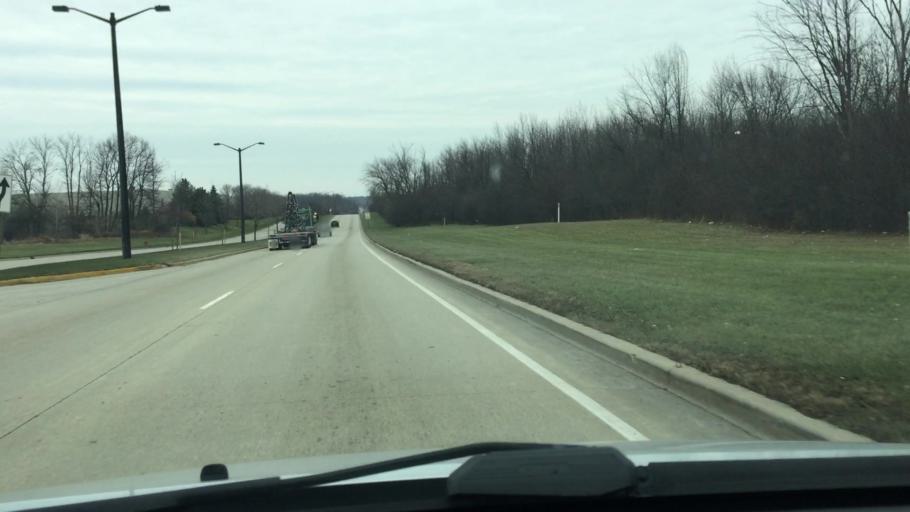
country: US
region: Wisconsin
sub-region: Waukesha County
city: Menomonee Falls
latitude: 43.1685
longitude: -88.0641
